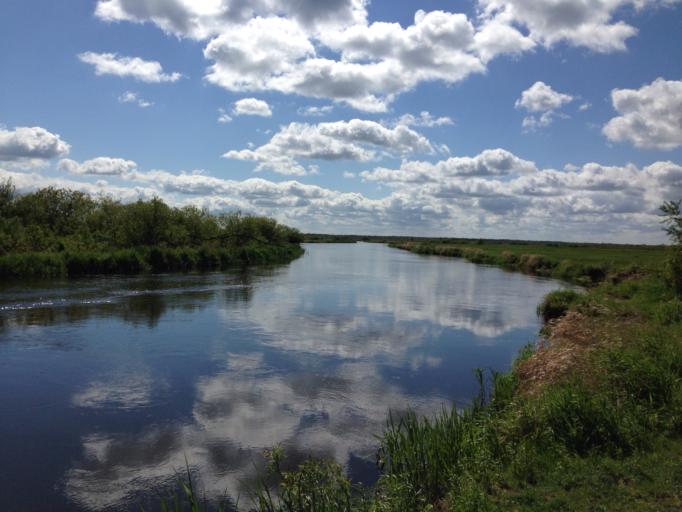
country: PL
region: Podlasie
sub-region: Powiat lomzynski
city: Wizna
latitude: 53.2842
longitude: 22.4649
